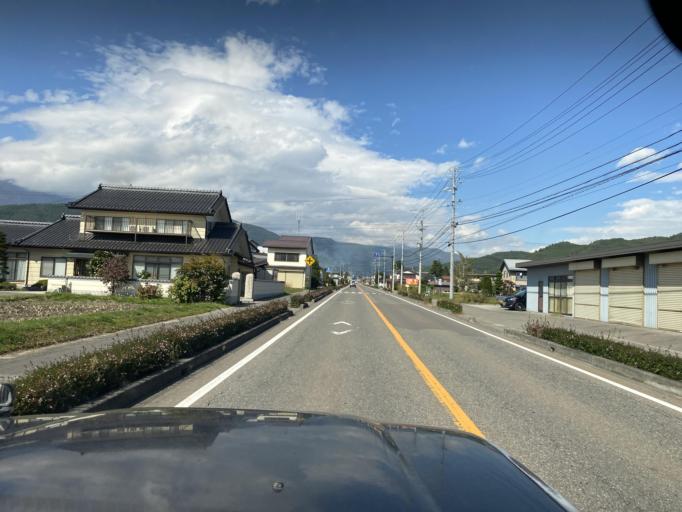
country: JP
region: Nagano
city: Omachi
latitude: 36.5241
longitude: 137.8513
